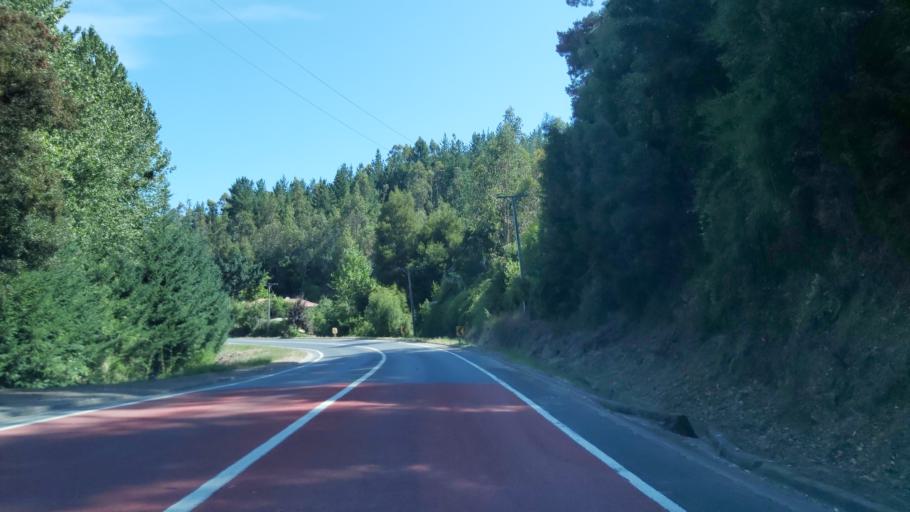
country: CL
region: Biobio
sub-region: Provincia de Concepcion
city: Lota
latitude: -37.1188
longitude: -72.9844
